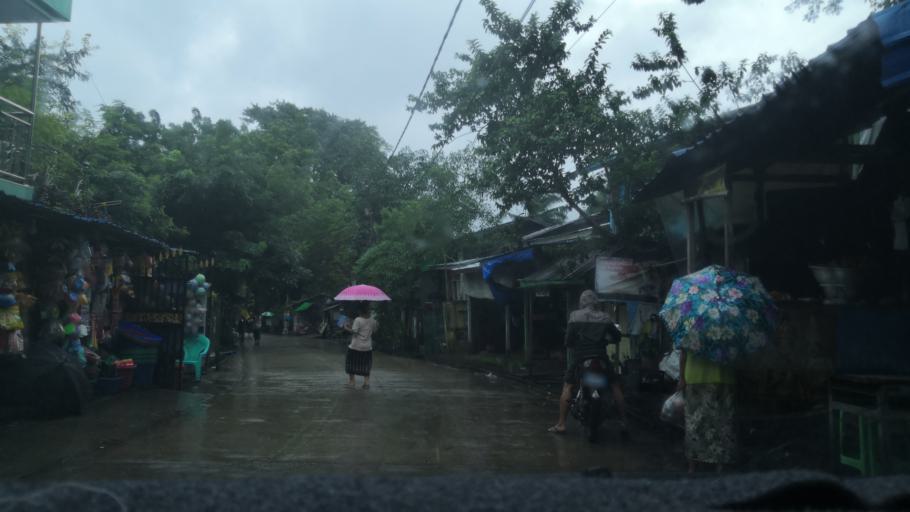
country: MM
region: Yangon
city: Yangon
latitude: 16.8779
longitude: 96.1492
